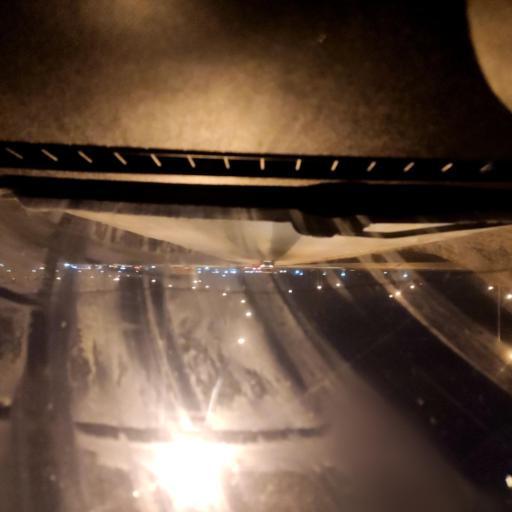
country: RU
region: Bashkortostan
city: Kabakovo
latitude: 54.4942
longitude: 55.9088
